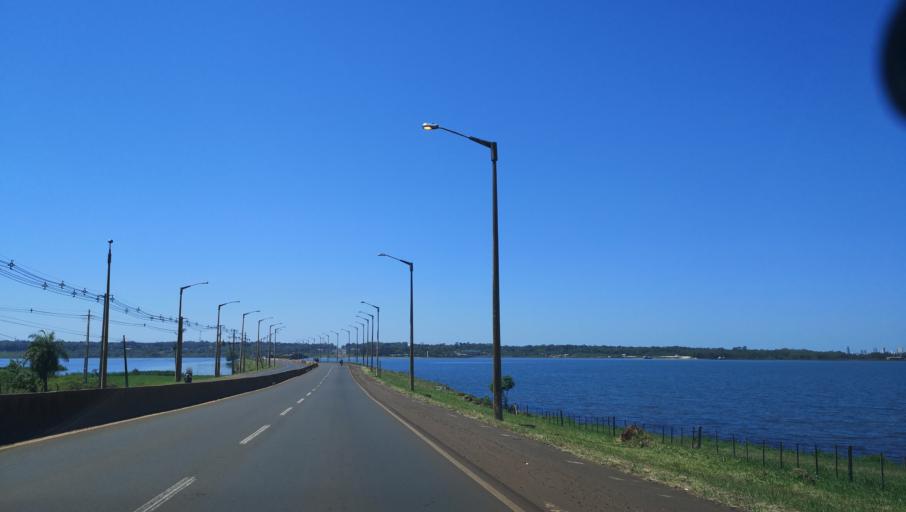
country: PY
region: Itapua
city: San Juan del Parana
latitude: -27.2935
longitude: -55.9118
